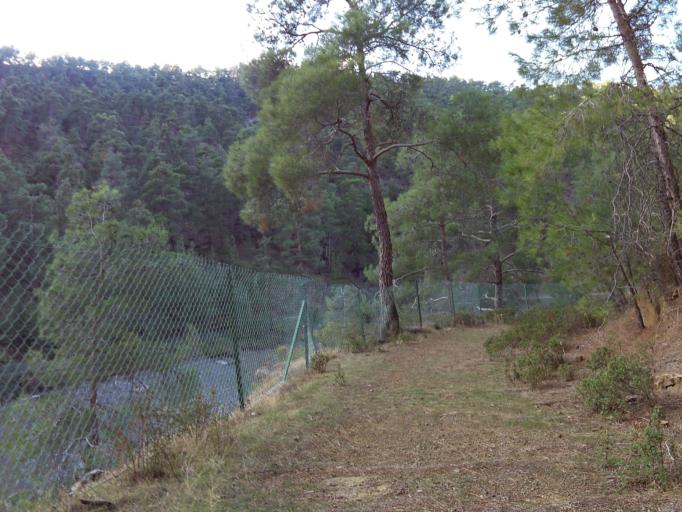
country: CY
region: Limassol
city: Kyperounta
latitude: 35.0038
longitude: 33.0382
